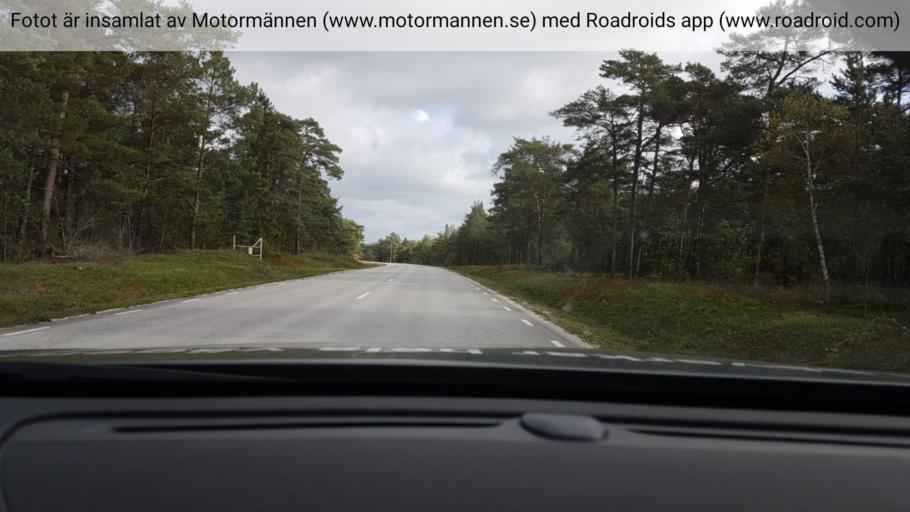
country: SE
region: Gotland
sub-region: Gotland
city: Slite
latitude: 57.7567
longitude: 18.7562
